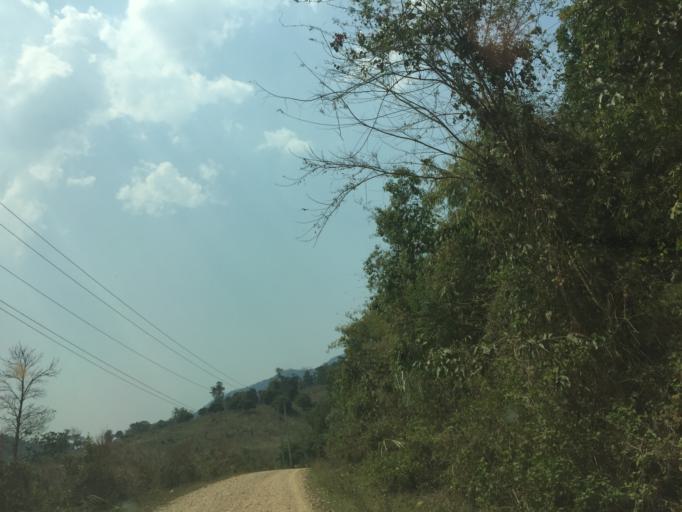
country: TH
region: Nan
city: Song Khwae
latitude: 19.7368
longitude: 100.7221
